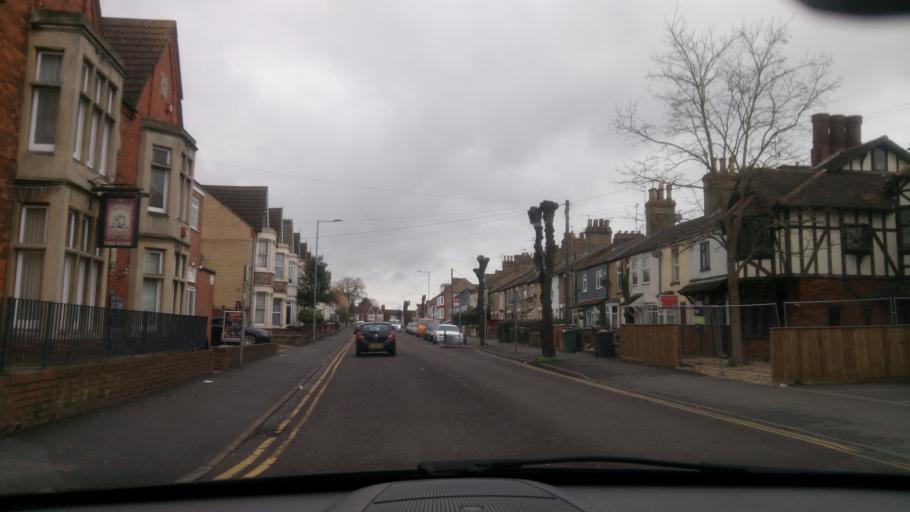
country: GB
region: England
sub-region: Peterborough
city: Peterborough
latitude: 52.5799
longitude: -0.2400
